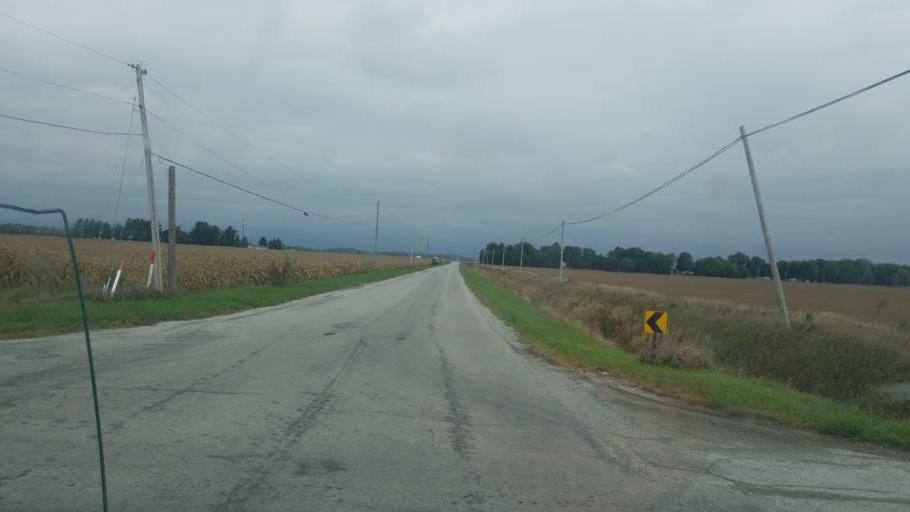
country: US
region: Ohio
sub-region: Wood County
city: Bowling Green
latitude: 41.3269
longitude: -83.6700
